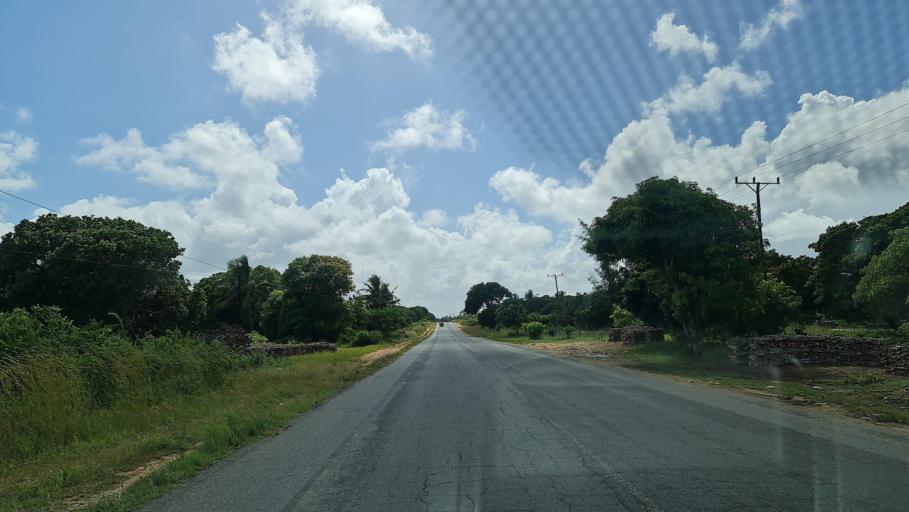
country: MZ
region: Gaza
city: Manjacaze
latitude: -24.6762
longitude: 34.5655
